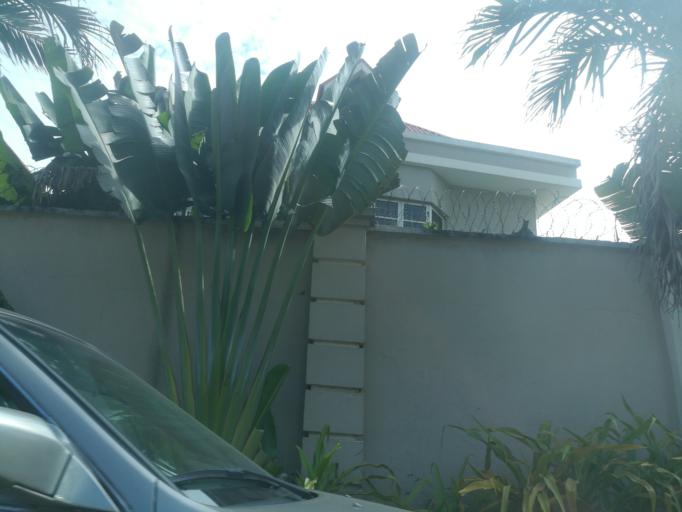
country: NG
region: Lagos
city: Ojota
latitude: 6.5774
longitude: 3.3669
